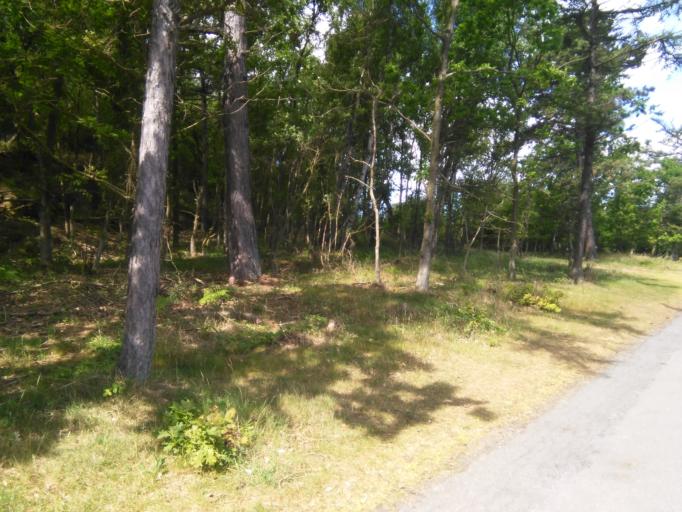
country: DK
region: Capital Region
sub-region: Bornholm Kommune
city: Ronne
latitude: 55.2973
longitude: 14.7750
